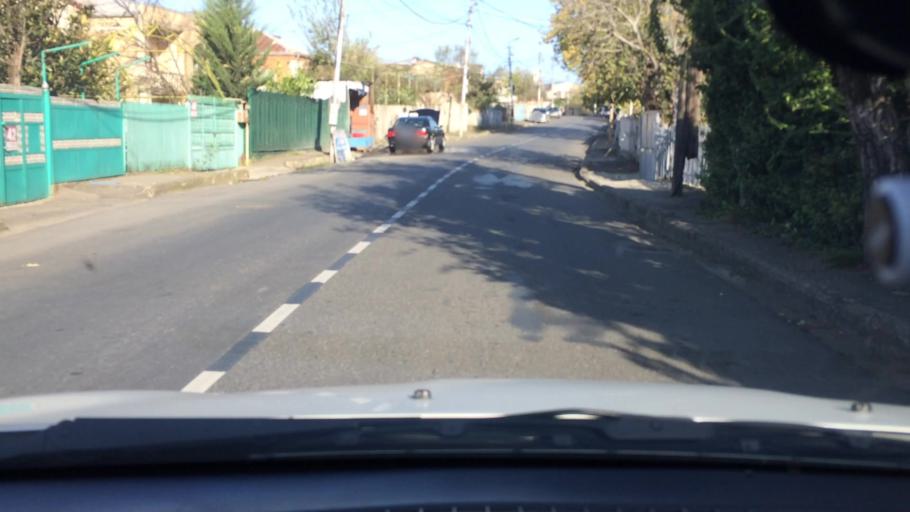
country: GE
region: Imereti
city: Kutaisi
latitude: 42.2697
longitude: 42.7143
